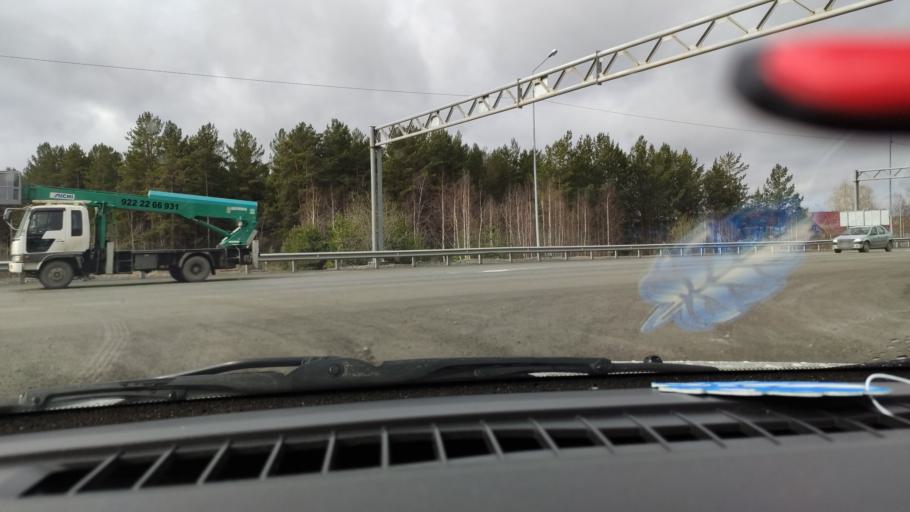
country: RU
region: Sverdlovsk
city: Talitsa
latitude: 56.8743
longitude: 60.0324
